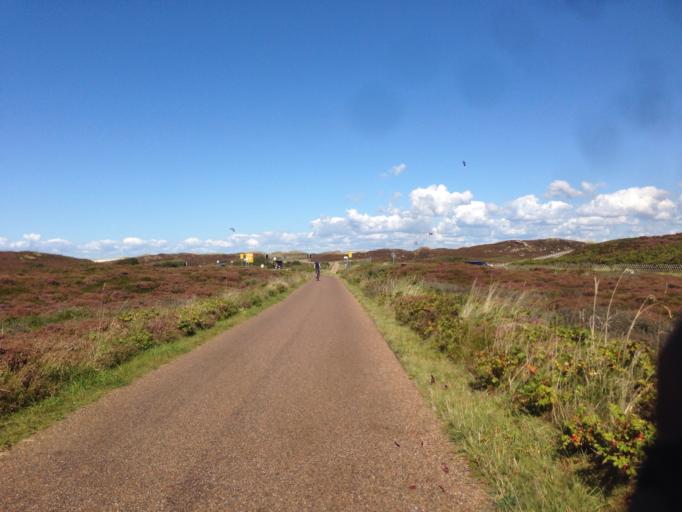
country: DE
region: Schleswig-Holstein
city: List
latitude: 55.0008
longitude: 8.3787
